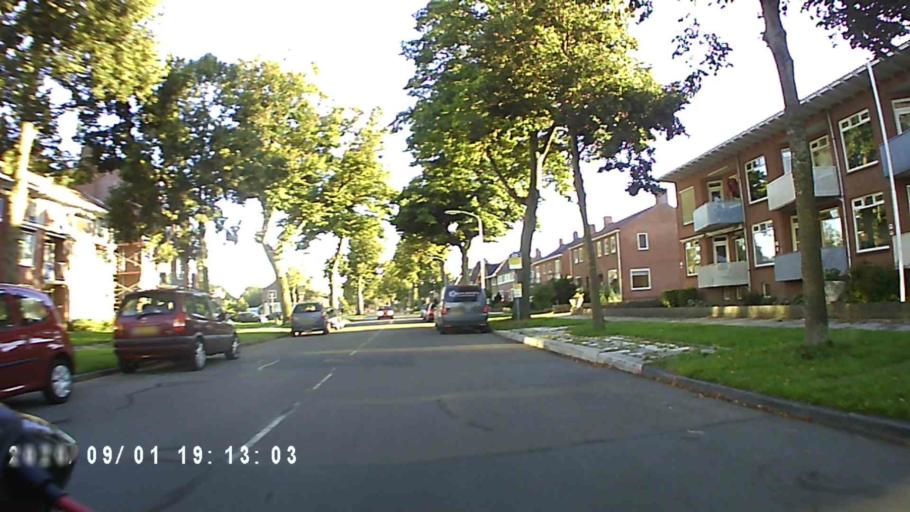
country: NL
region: Groningen
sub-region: Gemeente Veendam
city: Veendam
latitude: 53.1021
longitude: 6.8718
